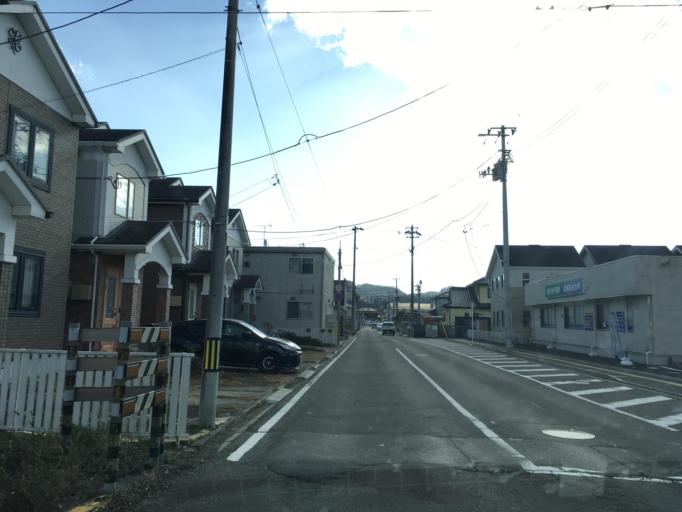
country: JP
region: Miyagi
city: Sendai
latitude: 38.2728
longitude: 140.7645
